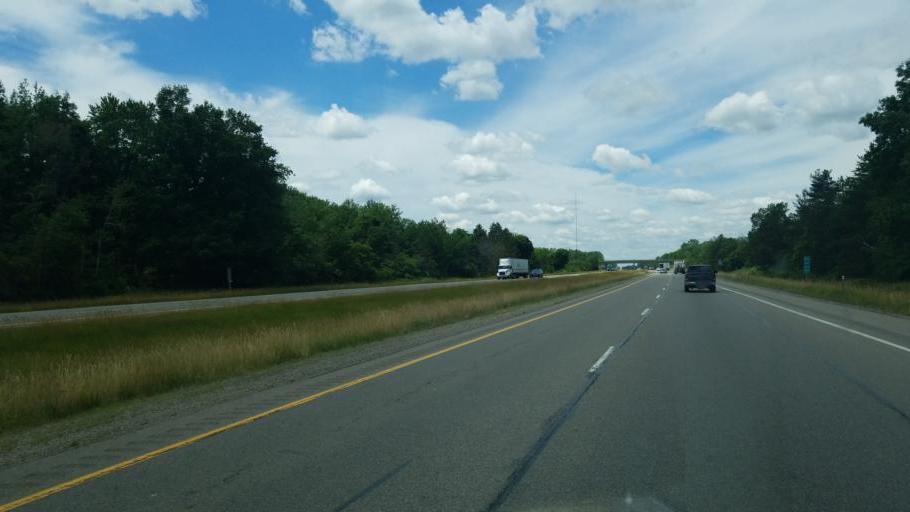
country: US
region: Michigan
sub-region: Eaton County
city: Dimondale
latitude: 42.6656
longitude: -84.5961
